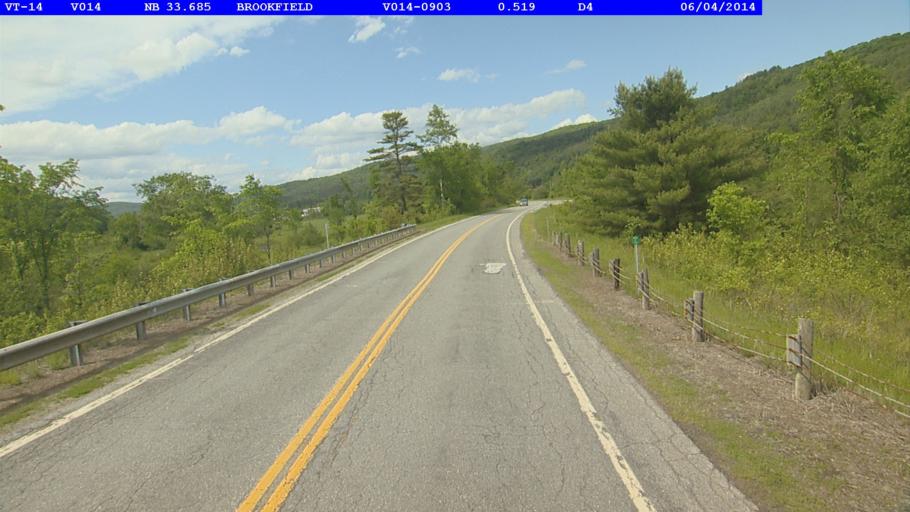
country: US
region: Vermont
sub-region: Orange County
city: Chelsea
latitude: 43.9865
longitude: -72.5571
